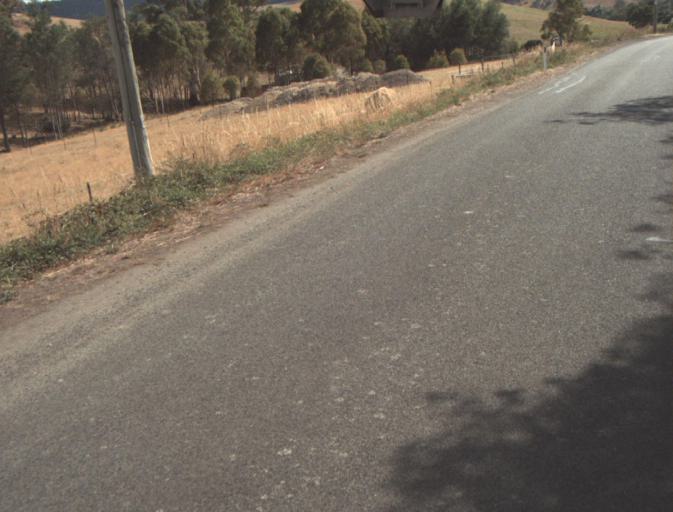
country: AU
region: Tasmania
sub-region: Launceston
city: Mayfield
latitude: -41.2574
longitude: 147.2086
